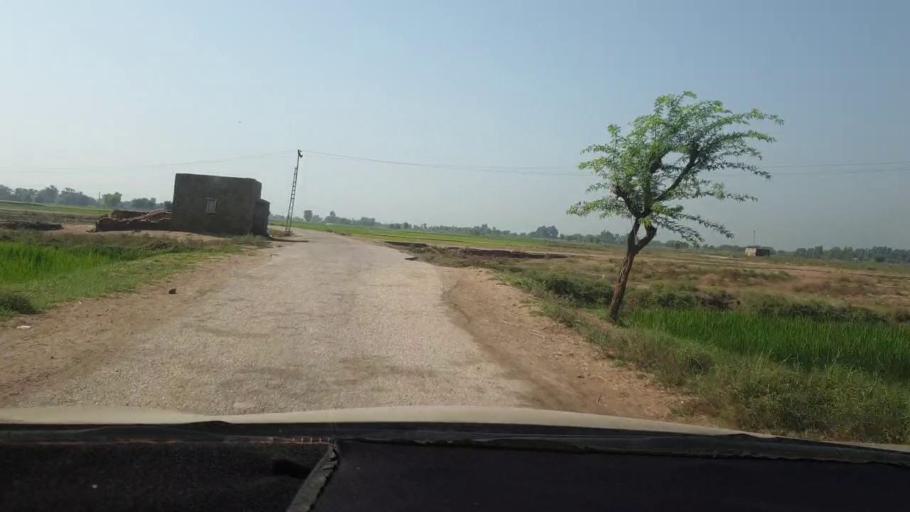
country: PK
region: Sindh
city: Miro Khan
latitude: 27.7311
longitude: 68.1184
